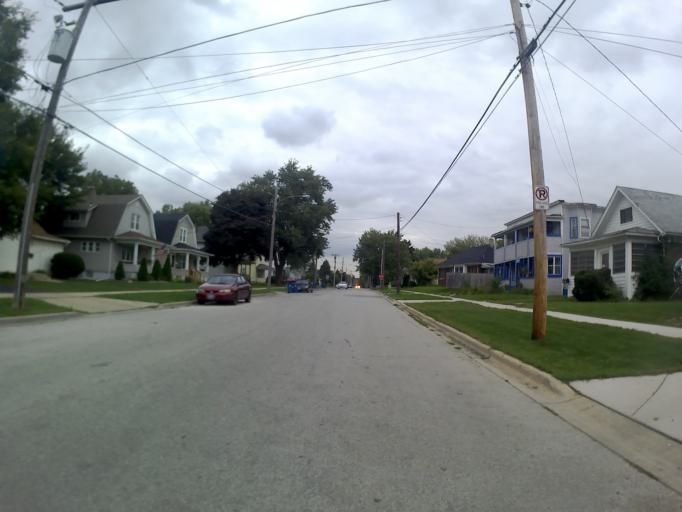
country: US
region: Illinois
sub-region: Kane County
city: Aurora
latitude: 41.7502
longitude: -88.3332
